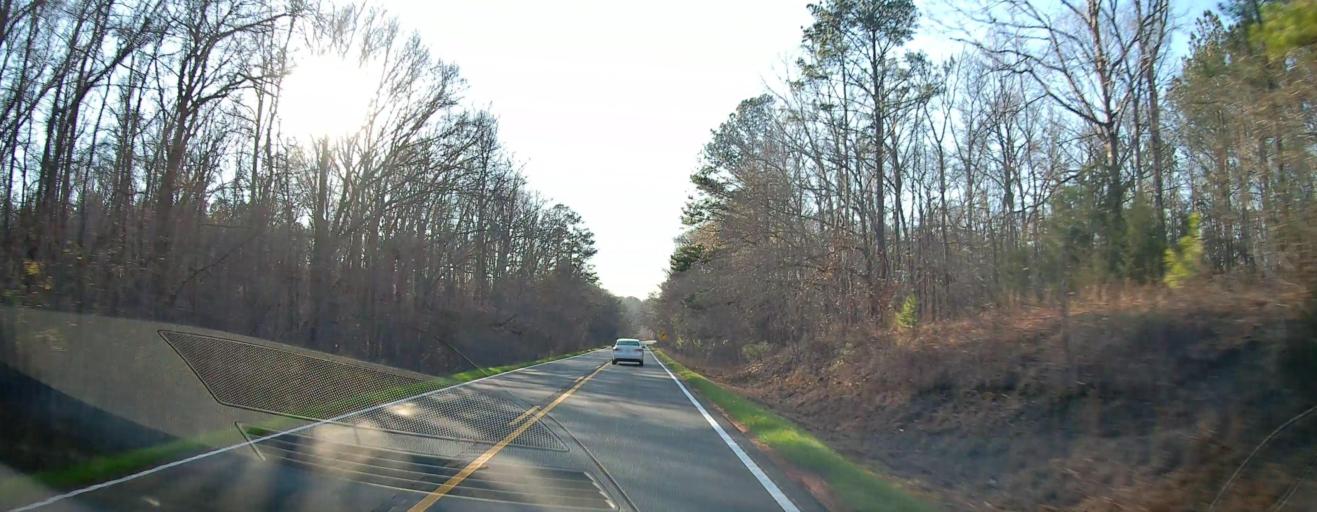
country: US
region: Georgia
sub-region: Harris County
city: Pine Mountain
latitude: 32.9151
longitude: -84.7566
